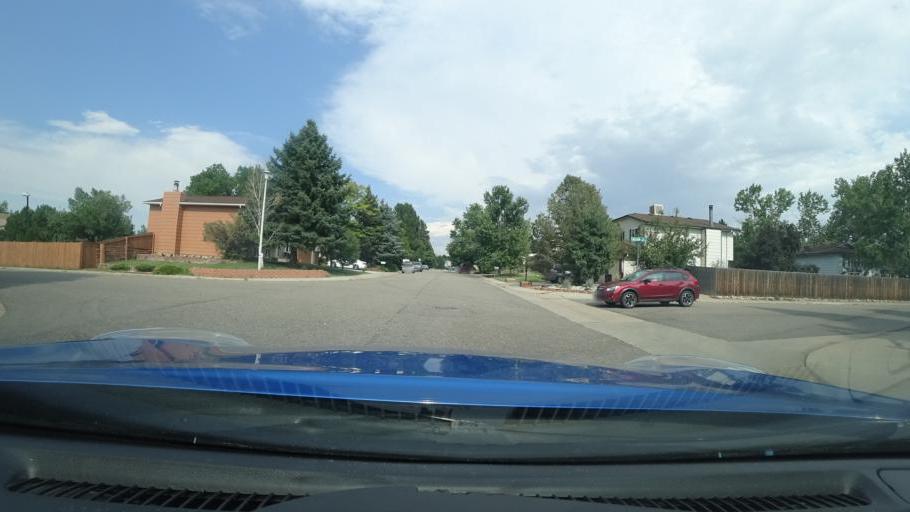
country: US
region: Colorado
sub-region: Adams County
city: Aurora
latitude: 39.6890
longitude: -104.7965
